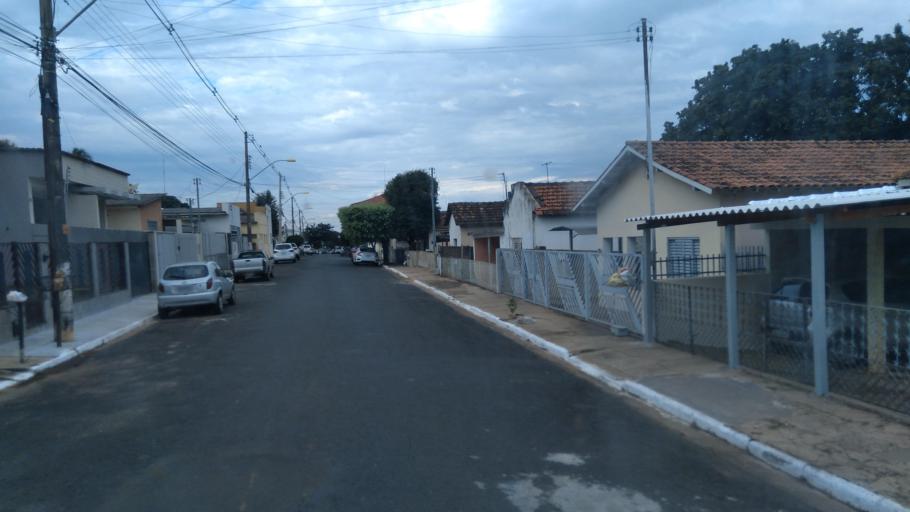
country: BR
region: Goias
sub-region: Mineiros
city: Mineiros
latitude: -17.5679
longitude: -52.5569
